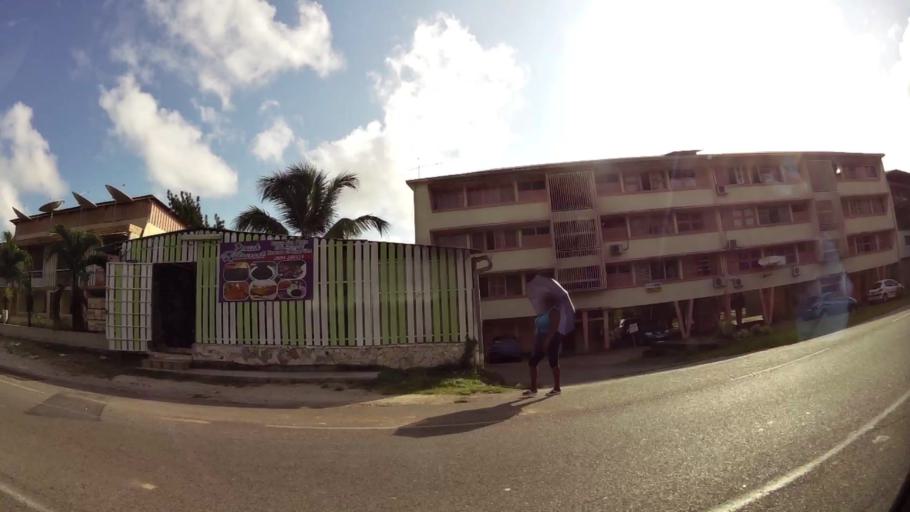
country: GF
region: Guyane
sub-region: Guyane
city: Cayenne
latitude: 4.9410
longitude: -52.3208
